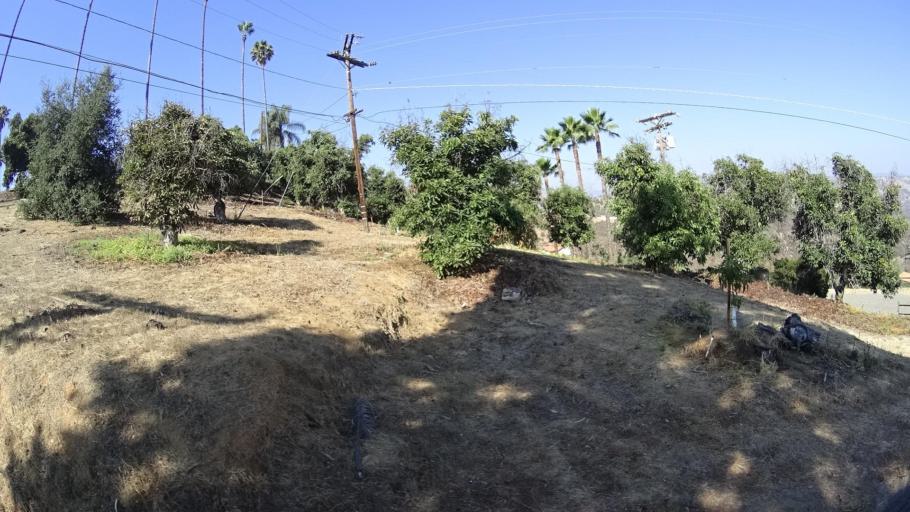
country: US
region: California
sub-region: San Diego County
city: Fallbrook
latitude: 33.4007
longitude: -117.2331
